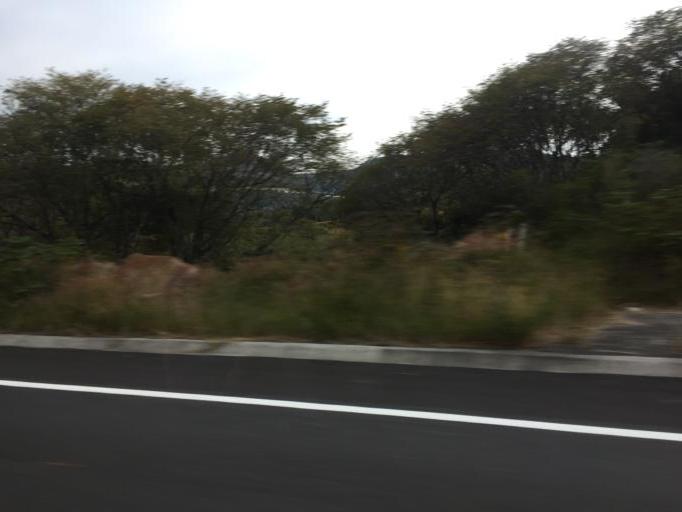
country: MX
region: Michoacan
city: Copandaro de Galeana
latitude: 19.8850
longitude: -101.2262
